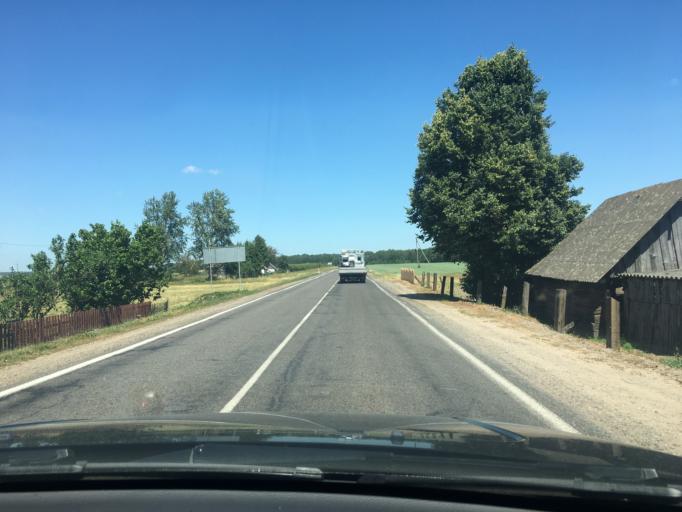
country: BY
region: Grodnenskaya
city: Iwye
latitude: 54.0654
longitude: 25.9113
